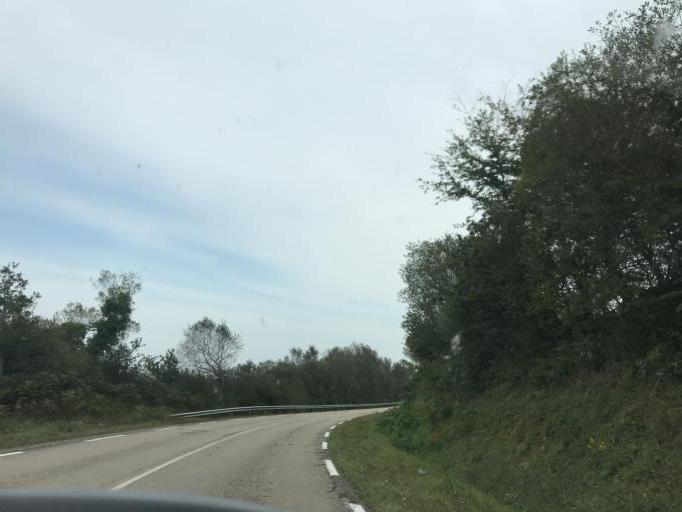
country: FR
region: Brittany
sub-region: Departement du Finistere
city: Plouneour-Menez
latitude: 48.3662
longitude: -3.8503
